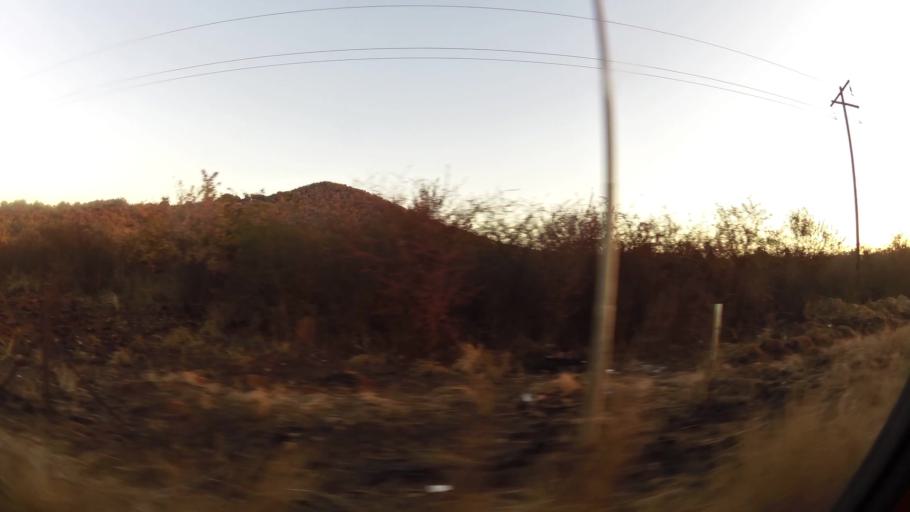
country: ZA
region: North-West
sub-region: Bojanala Platinum District Municipality
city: Rustenburg
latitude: -25.6079
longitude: 27.1847
